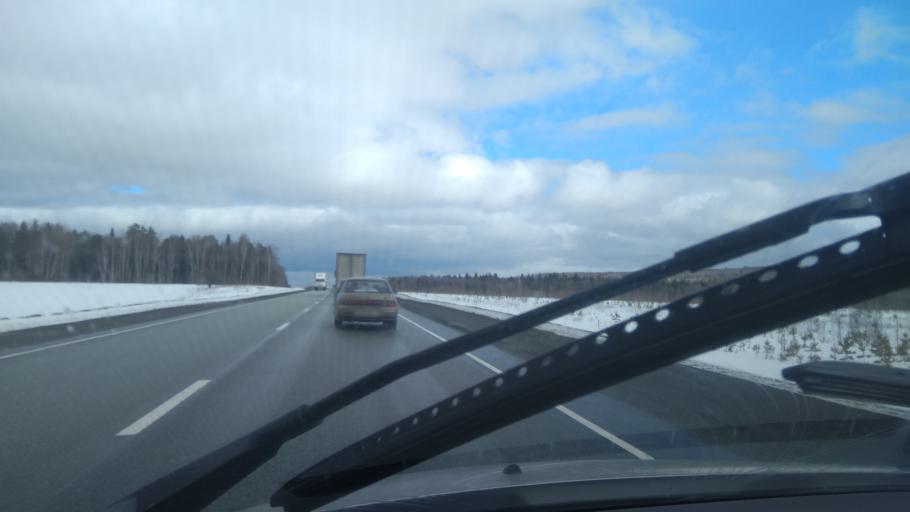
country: RU
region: Sverdlovsk
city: Bisert'
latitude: 56.8115
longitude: 58.7368
